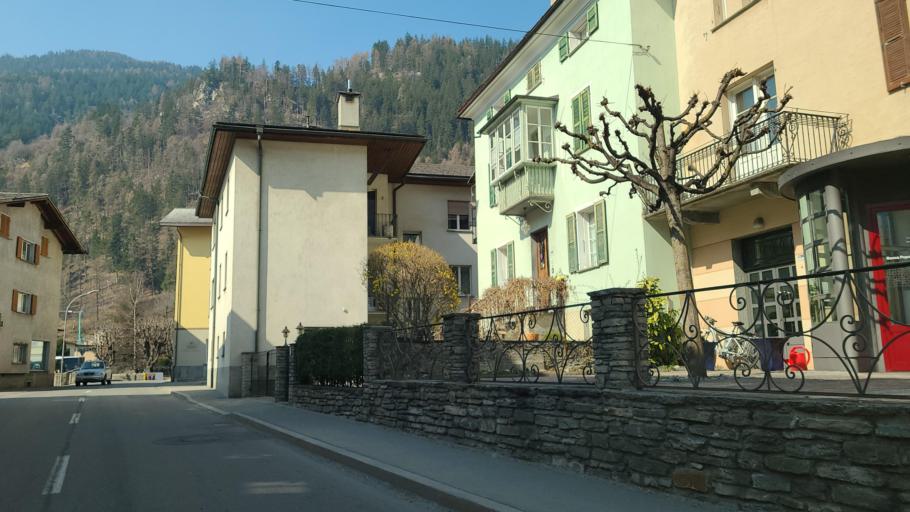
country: CH
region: Grisons
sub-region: Bernina District
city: Poschiavo
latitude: 46.3239
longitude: 10.0571
